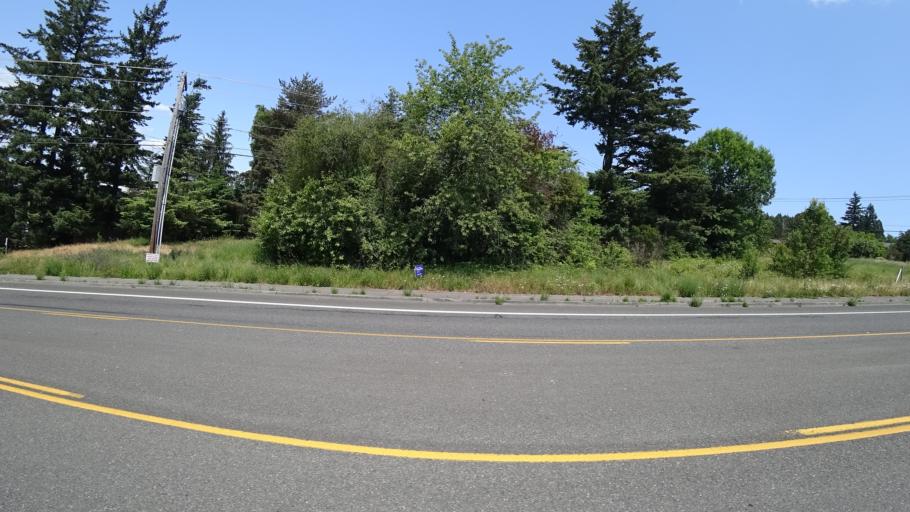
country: US
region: Oregon
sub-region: Multnomah County
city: Lents
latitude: 45.4511
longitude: -122.5699
